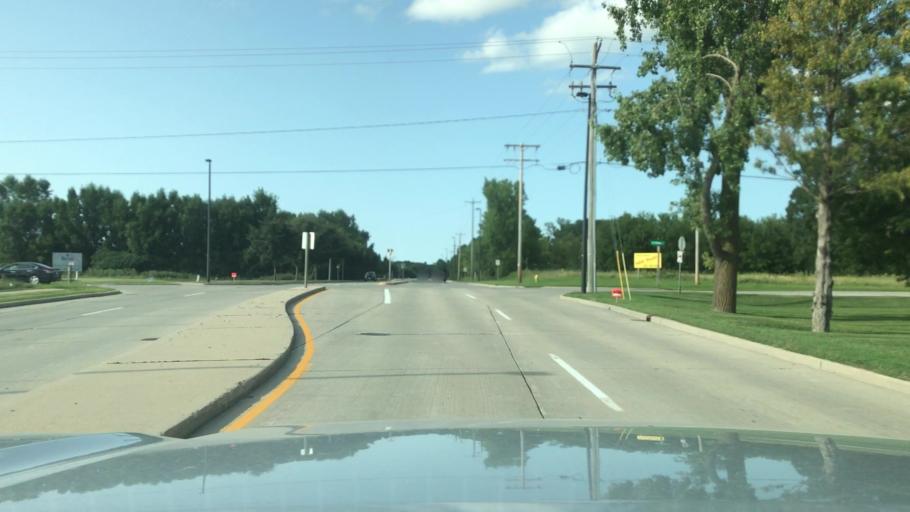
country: US
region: Wisconsin
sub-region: Brown County
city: Bellevue
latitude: 44.4876
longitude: -87.9178
